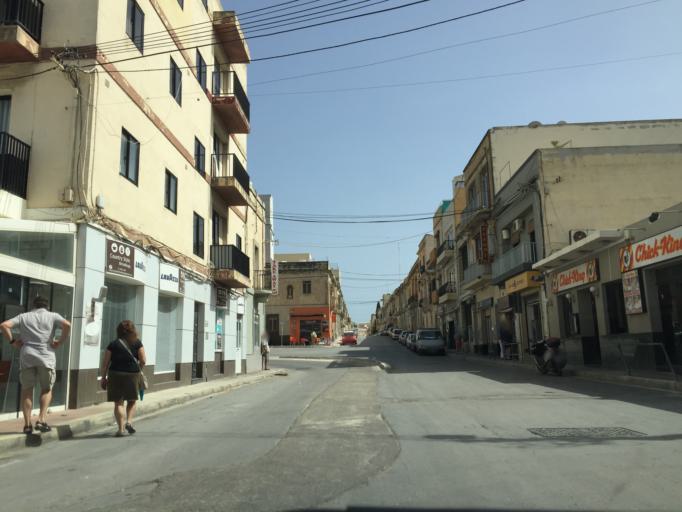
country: MT
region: Birzebbuga
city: Birzebbuga
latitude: 35.8239
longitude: 14.5284
